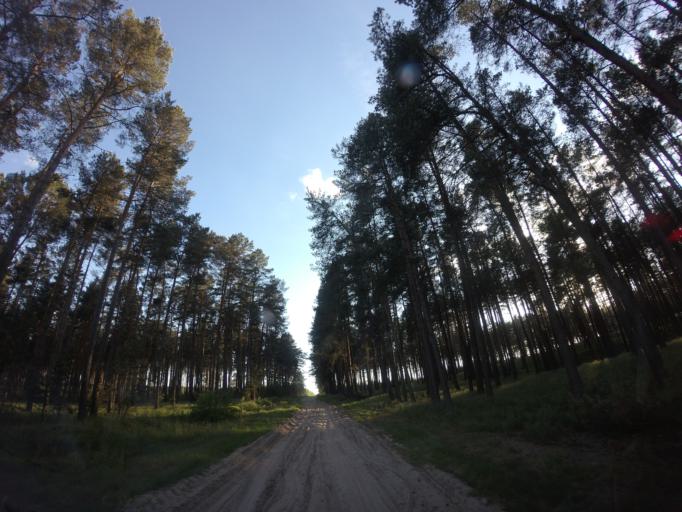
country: PL
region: West Pomeranian Voivodeship
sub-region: Powiat choszczenski
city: Drawno
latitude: 53.1570
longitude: 15.7301
